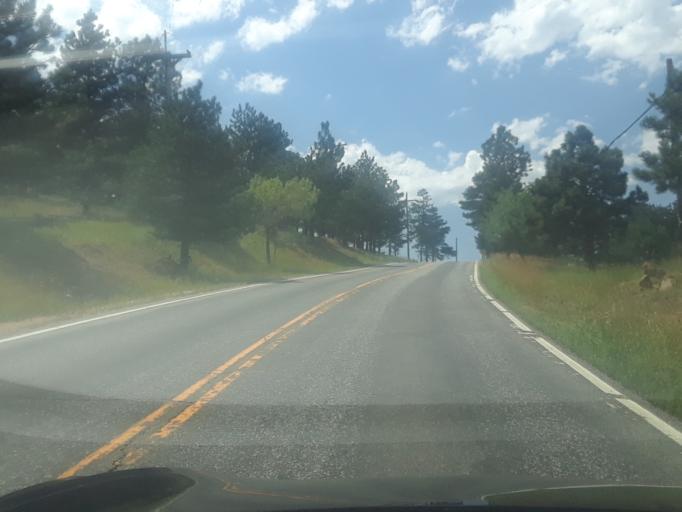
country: US
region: Colorado
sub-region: Boulder County
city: Boulder
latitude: 40.0480
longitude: -105.3421
